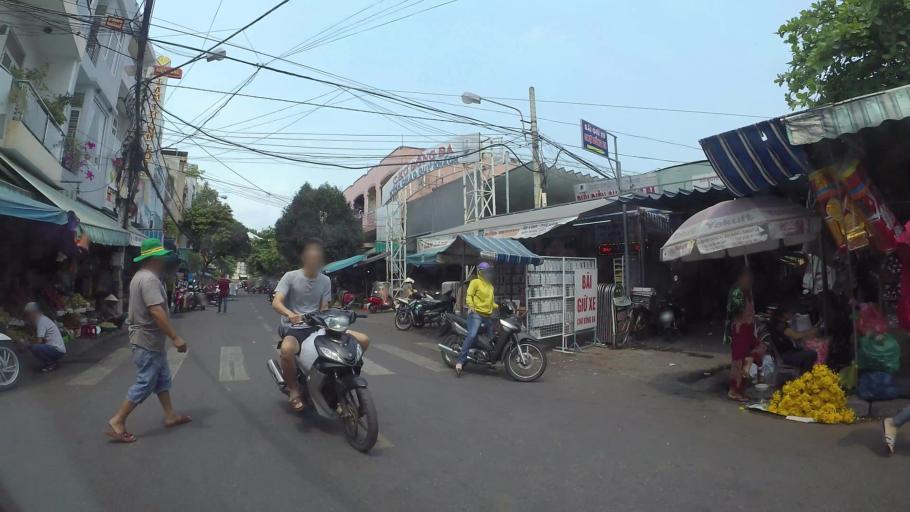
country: VN
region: Da Nang
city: Da Nang
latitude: 16.0811
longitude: 108.2176
